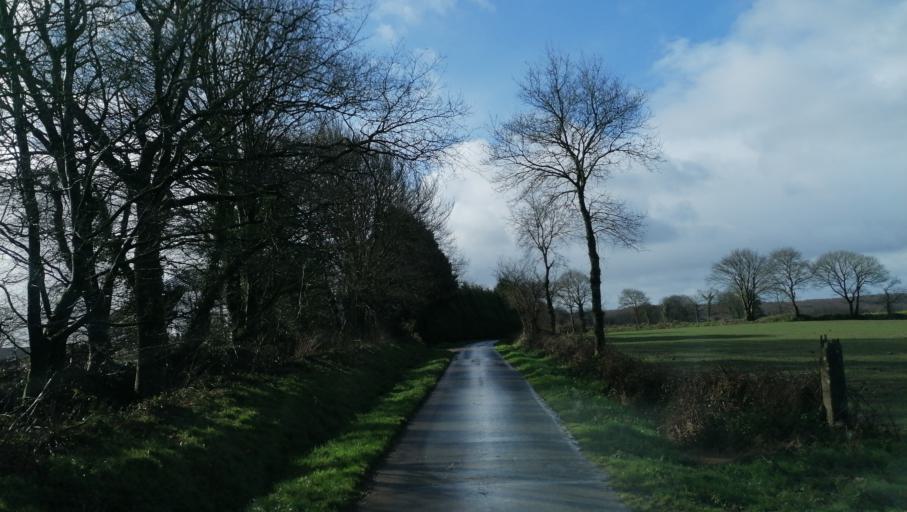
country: FR
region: Brittany
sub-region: Departement des Cotes-d'Armor
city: Lanrodec
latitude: 48.4891
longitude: -3.0208
